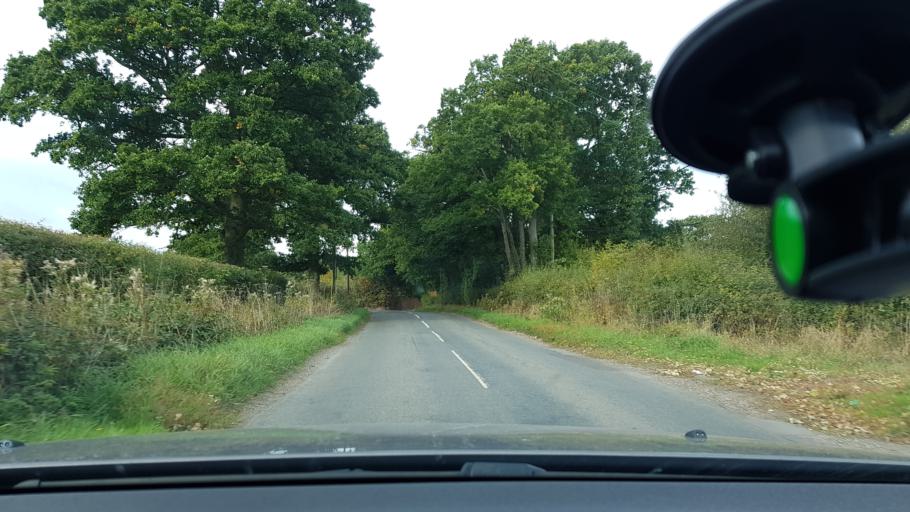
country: GB
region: England
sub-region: West Berkshire
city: Kintbury
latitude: 51.3891
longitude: -1.4181
